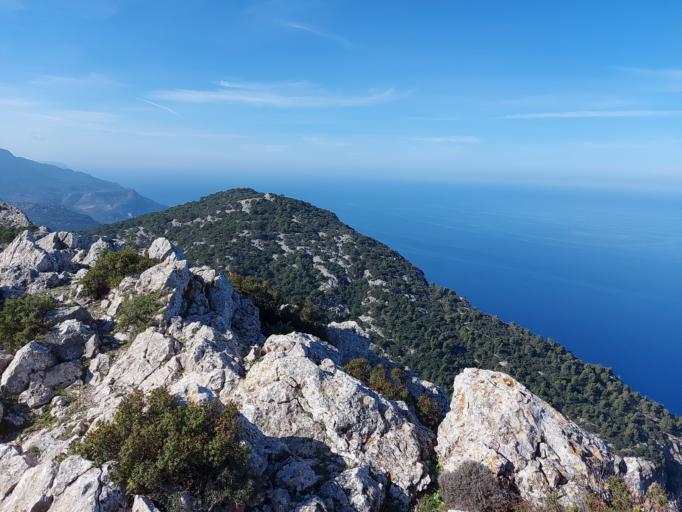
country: ES
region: Balearic Islands
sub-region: Illes Balears
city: Valldemossa
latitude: 39.7306
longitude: 2.6297
